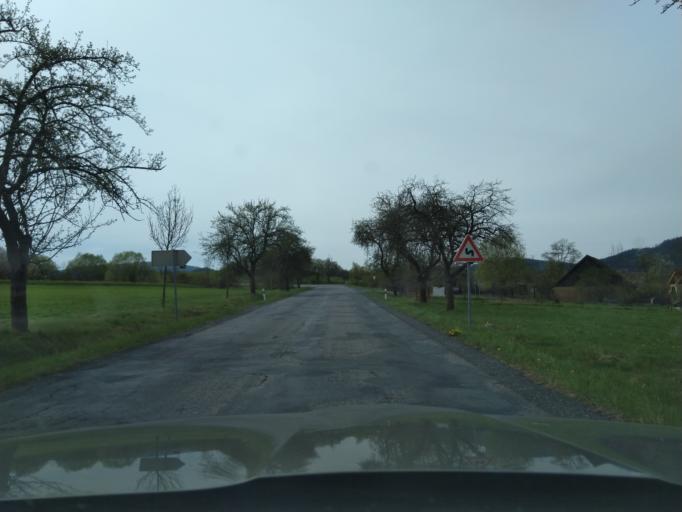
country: CZ
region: Plzensky
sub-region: Okres Klatovy
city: Kasperske Hory
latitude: 49.2054
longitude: 13.6121
